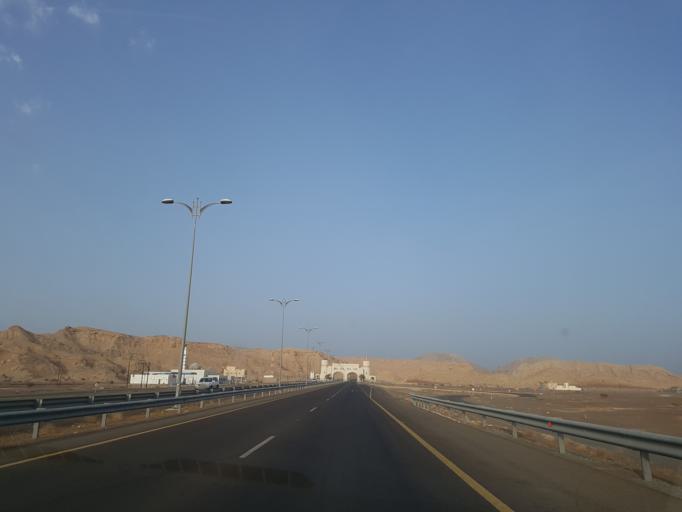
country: OM
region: Al Buraimi
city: Al Buraymi
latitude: 24.2319
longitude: 55.9298
